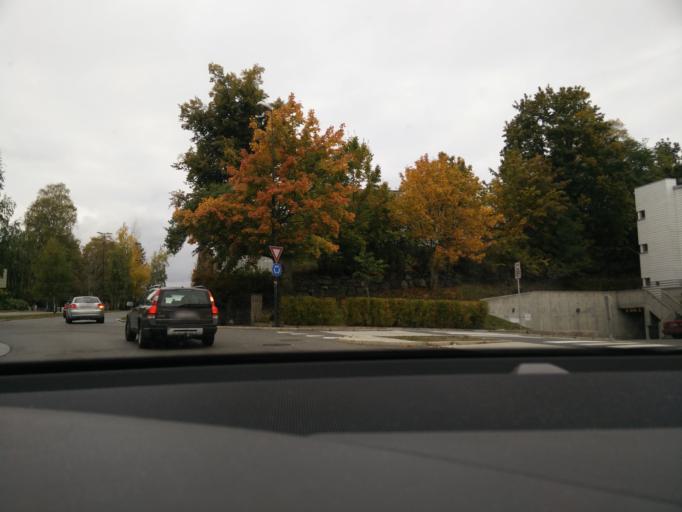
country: NO
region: Oslo
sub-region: Oslo
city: Sjolyststranda
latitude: 59.9322
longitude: 10.7062
